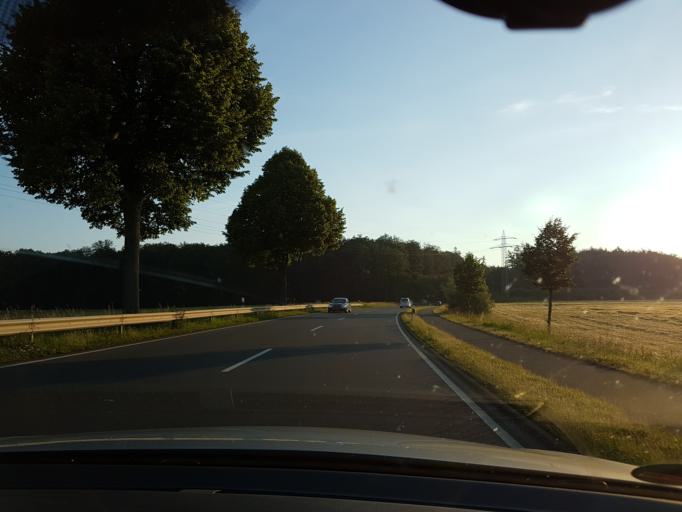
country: DE
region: Lower Saxony
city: Wolsdorf
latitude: 52.1997
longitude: 10.9683
